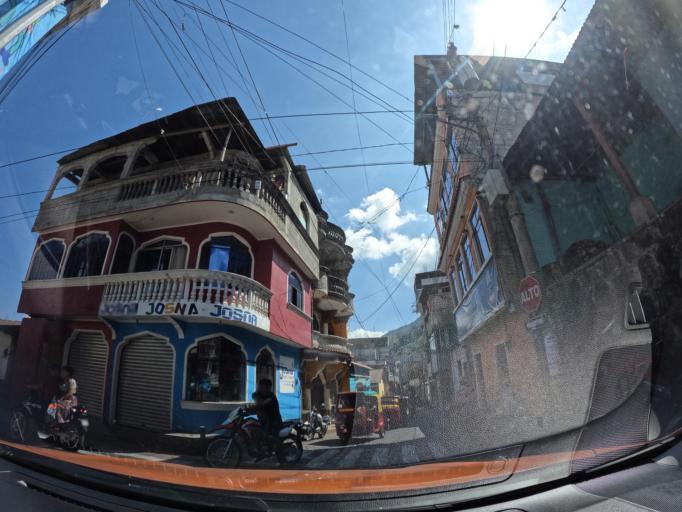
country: GT
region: Solola
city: San Pedro La Laguna
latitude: 14.6902
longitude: -91.2723
